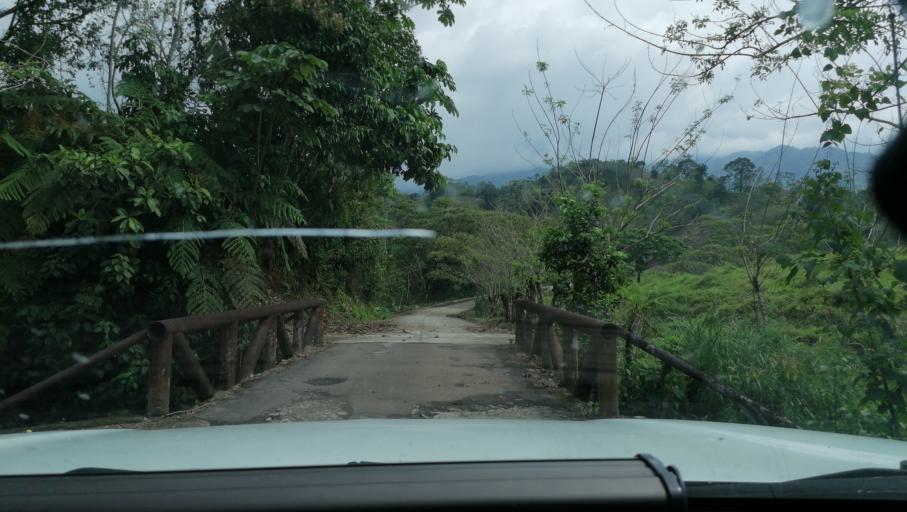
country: MX
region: Chiapas
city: Ocotepec
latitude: 17.3261
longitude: -93.1679
